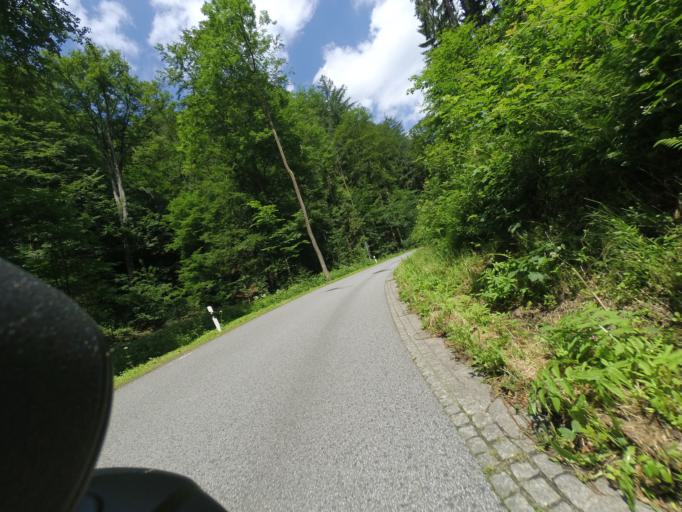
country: DE
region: Saxony
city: Porschdorf
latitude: 50.9536
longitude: 14.1310
